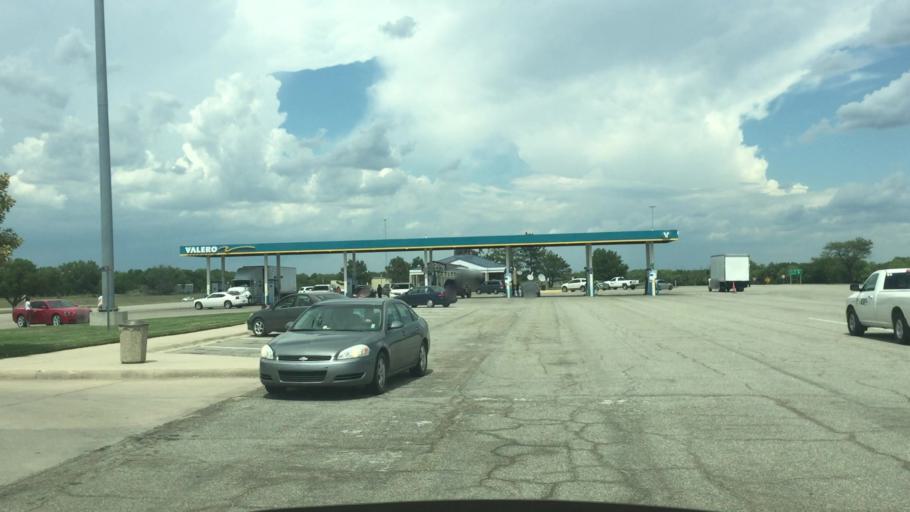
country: US
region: Kansas
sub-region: Lyon County
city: Emporia
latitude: 38.4705
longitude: -96.1850
